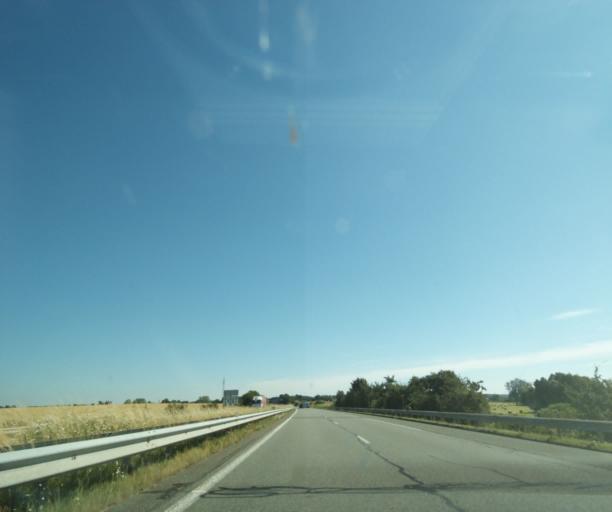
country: FR
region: Champagne-Ardenne
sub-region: Departement de la Haute-Marne
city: Avrecourt
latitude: 47.9862
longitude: 5.5082
